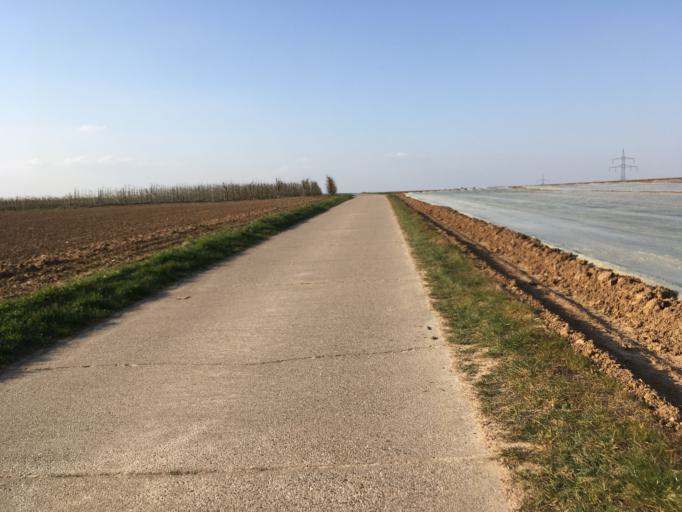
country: DE
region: Baden-Wuerttemberg
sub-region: Regierungsbezirk Stuttgart
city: Lauffen am Neckar
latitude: 49.0792
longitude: 9.1177
